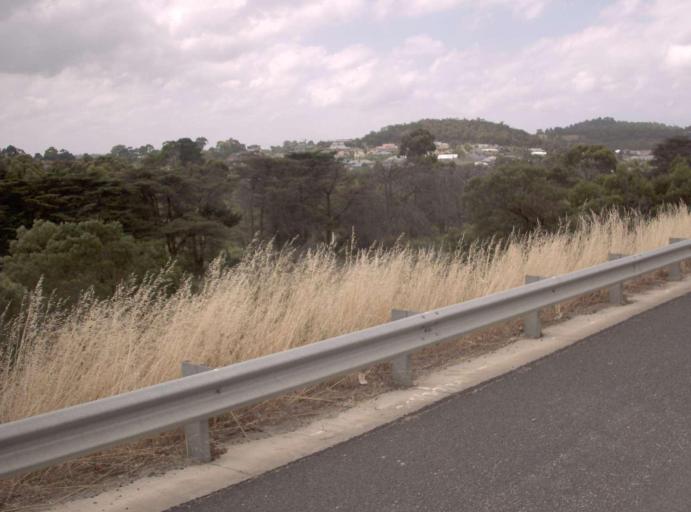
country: AU
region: Victoria
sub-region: Cardinia
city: Officer
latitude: -38.0565
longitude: 145.3784
